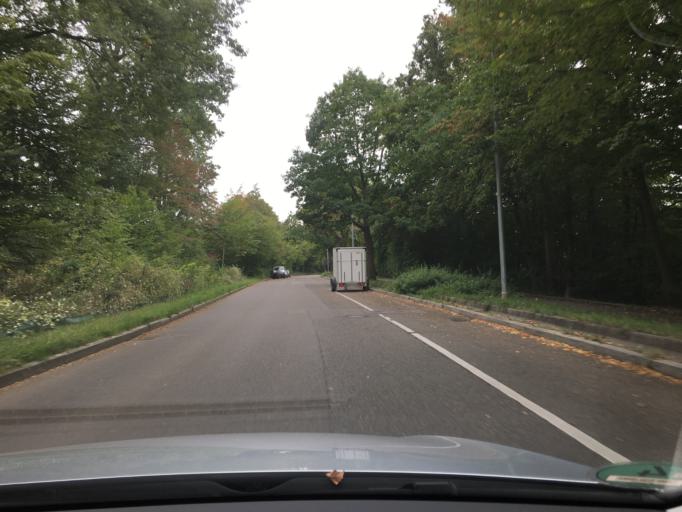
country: DE
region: Baden-Wuerttemberg
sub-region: Regierungsbezirk Stuttgart
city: Boeblingen
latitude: 48.6682
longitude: 8.9964
